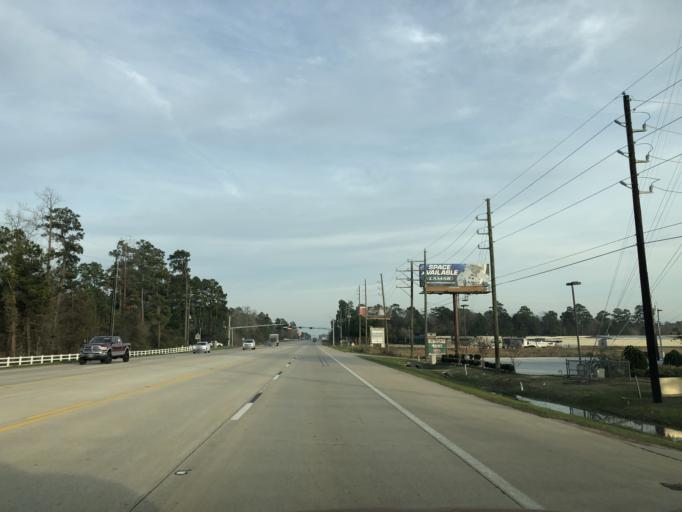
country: US
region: Texas
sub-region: Montgomery County
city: Pinehurst
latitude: 30.2211
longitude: -95.5944
